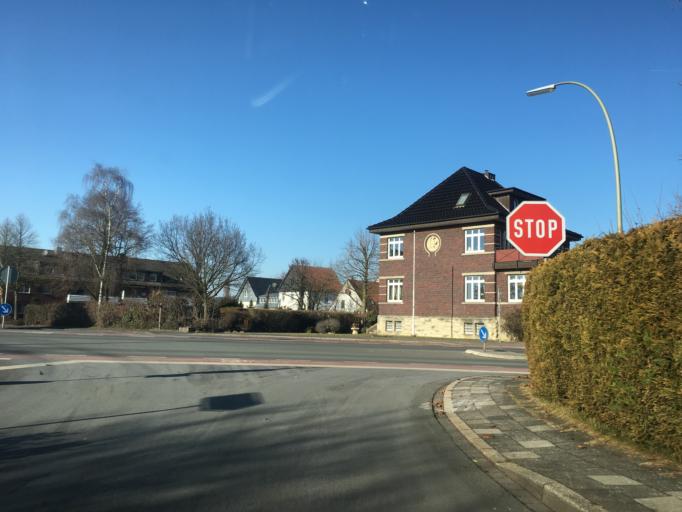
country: DE
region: North Rhine-Westphalia
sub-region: Regierungsbezirk Munster
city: Billerbeck
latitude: 51.9800
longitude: 7.2903
